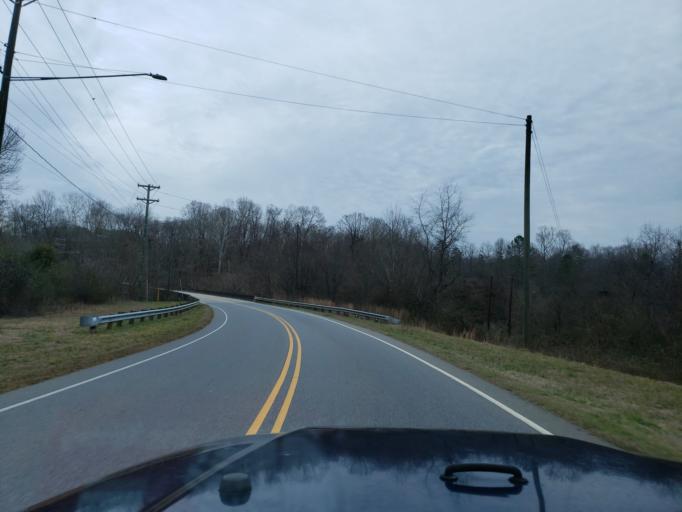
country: US
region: North Carolina
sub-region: Cleveland County
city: Shelby
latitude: 35.3027
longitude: -81.5670
